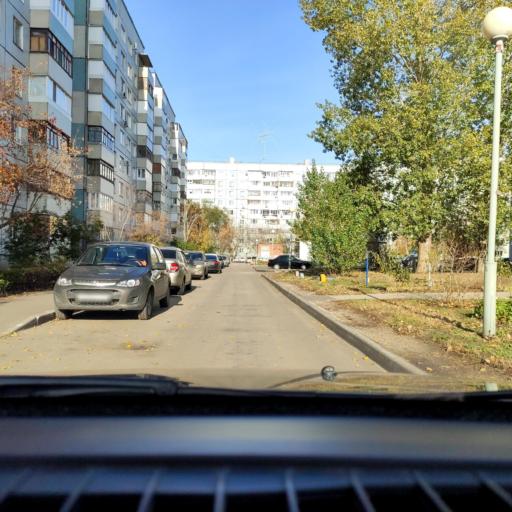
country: RU
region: Samara
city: Tol'yatti
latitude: 53.5455
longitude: 49.3525
